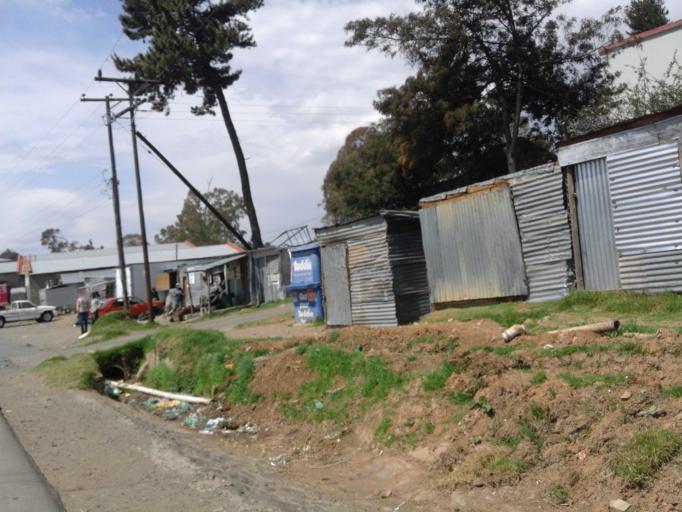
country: LS
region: Qacha's Nek
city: Qacha's Nek
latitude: -30.1172
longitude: 28.6838
